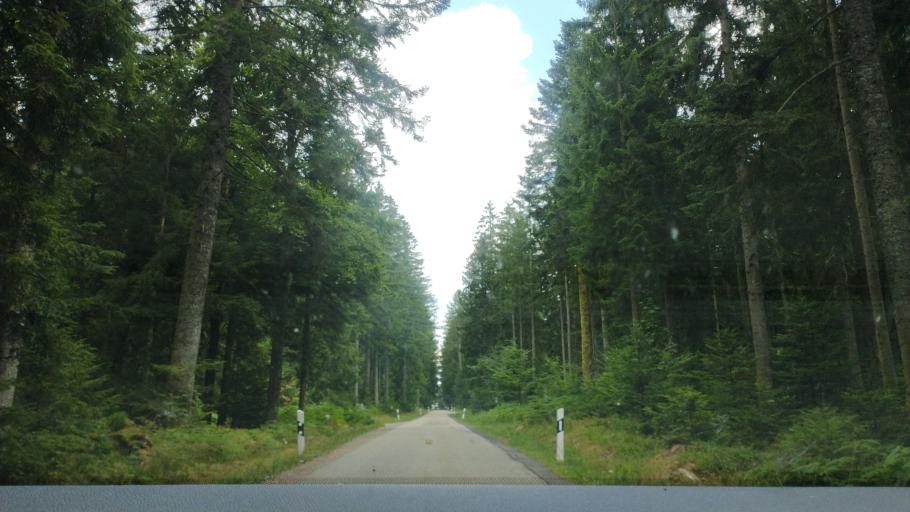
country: DE
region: Baden-Wuerttemberg
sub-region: Freiburg Region
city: Oppenau
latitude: 48.4372
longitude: 8.1459
